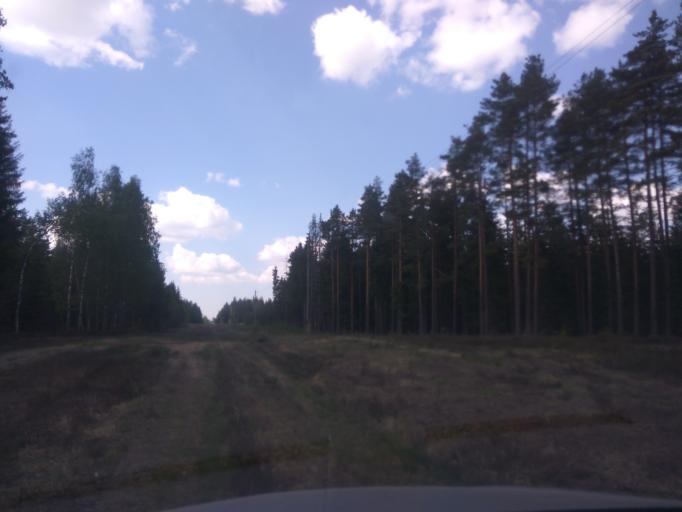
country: LV
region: Kuldigas Rajons
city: Kuldiga
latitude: 57.1832
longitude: 21.9974
